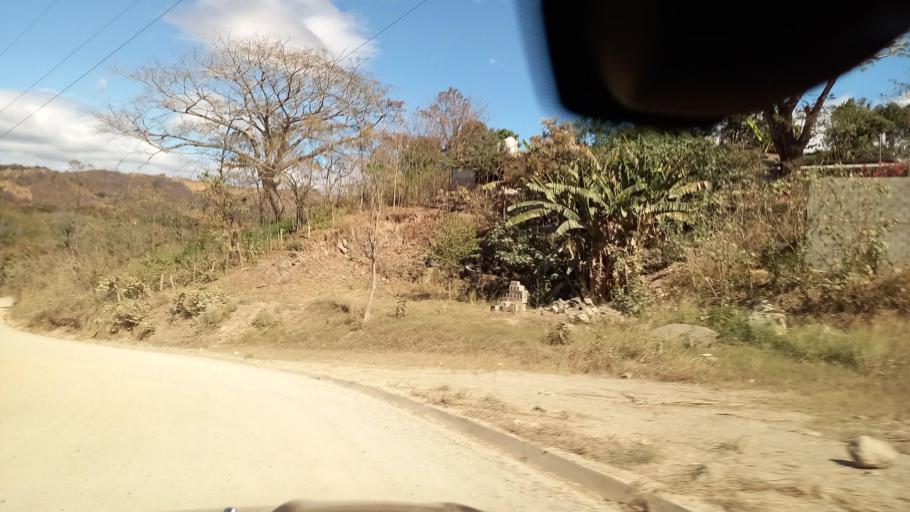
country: SV
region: Santa Ana
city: Metapan
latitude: 14.3593
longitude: -89.4536
